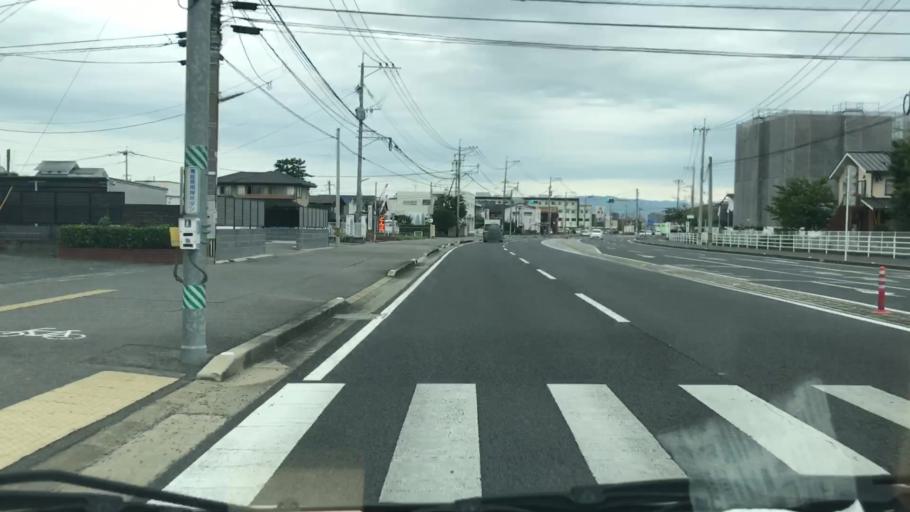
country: JP
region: Saga Prefecture
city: Saga-shi
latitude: 33.2339
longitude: 130.2936
